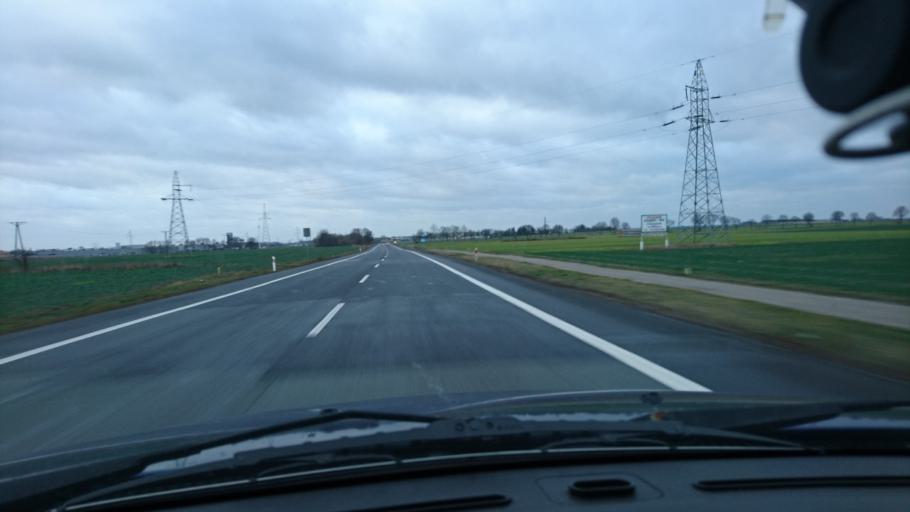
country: PL
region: Opole Voivodeship
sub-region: Powiat kluczborski
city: Kluczbork
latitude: 50.9903
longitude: 18.2249
